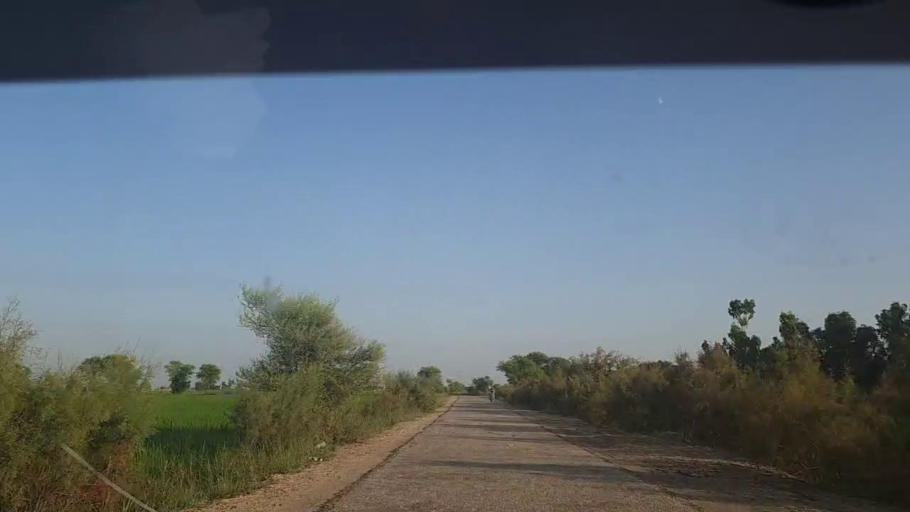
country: PK
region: Sindh
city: Thul
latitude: 28.2052
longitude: 68.8723
